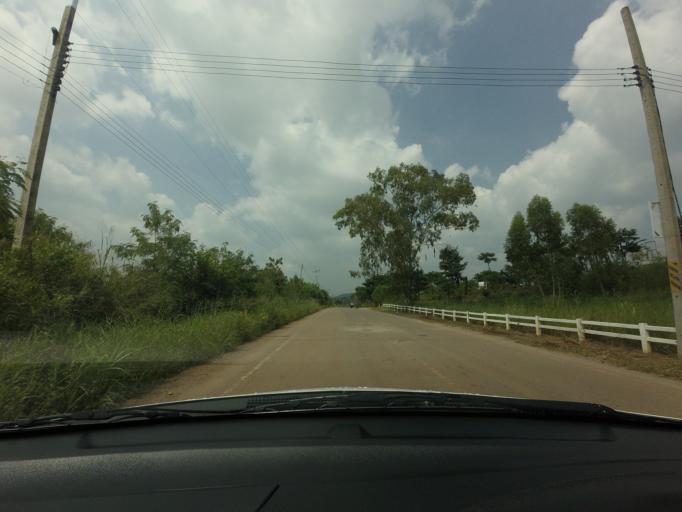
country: TH
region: Nakhon Ratchasima
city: Pak Chong
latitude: 14.5522
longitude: 101.5979
